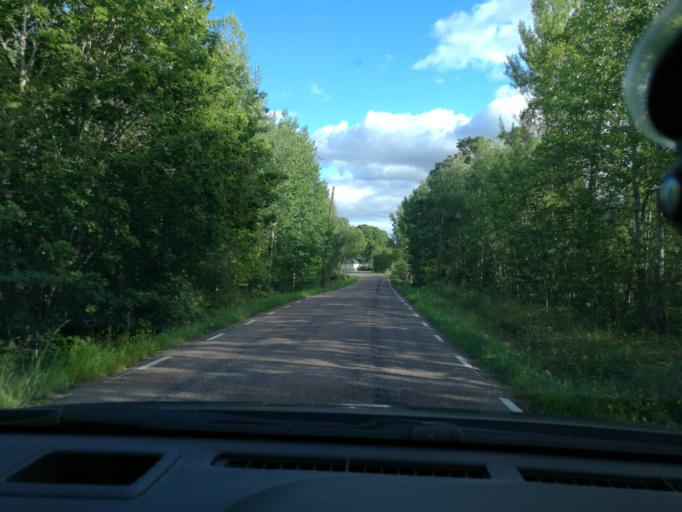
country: SE
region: Vaestmanland
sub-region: Hallstahammars Kommun
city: Kolback
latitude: 59.5393
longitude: 16.1342
